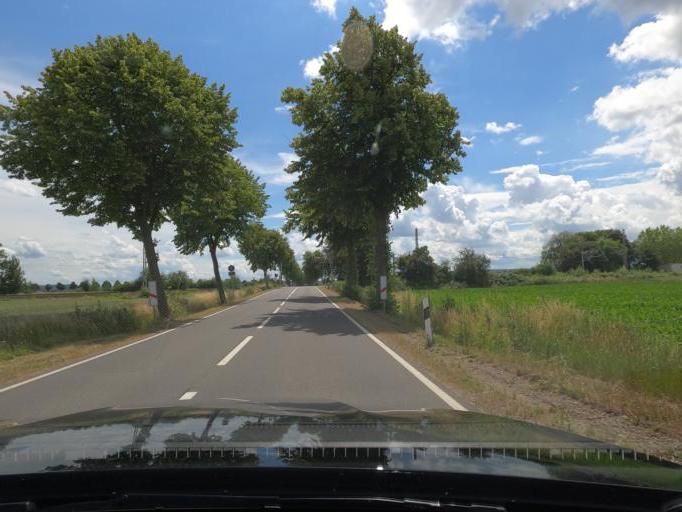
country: DE
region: Lower Saxony
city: Schellerten
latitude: 52.1799
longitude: 10.0413
